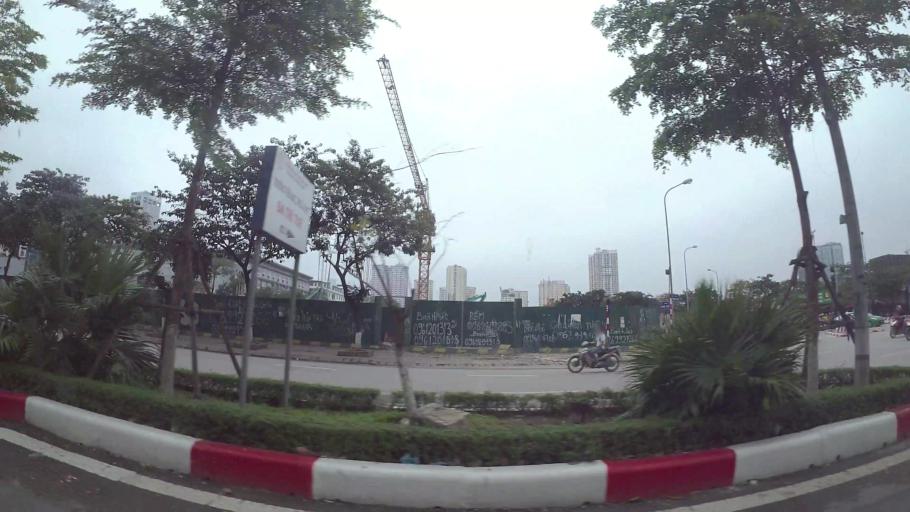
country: VN
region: Ha Noi
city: Cau Giay
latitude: 21.0305
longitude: 105.7884
